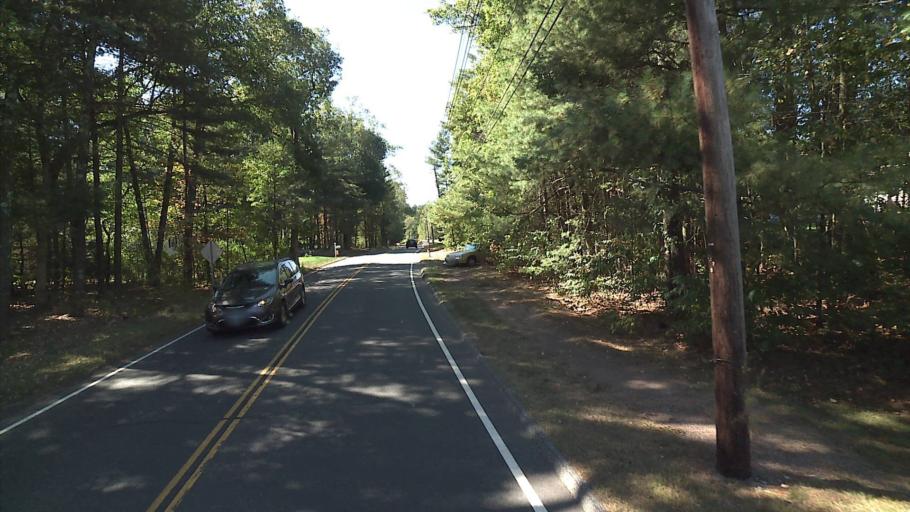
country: US
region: Connecticut
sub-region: Hartford County
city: Glastonbury Center
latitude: 41.6970
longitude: -72.5313
